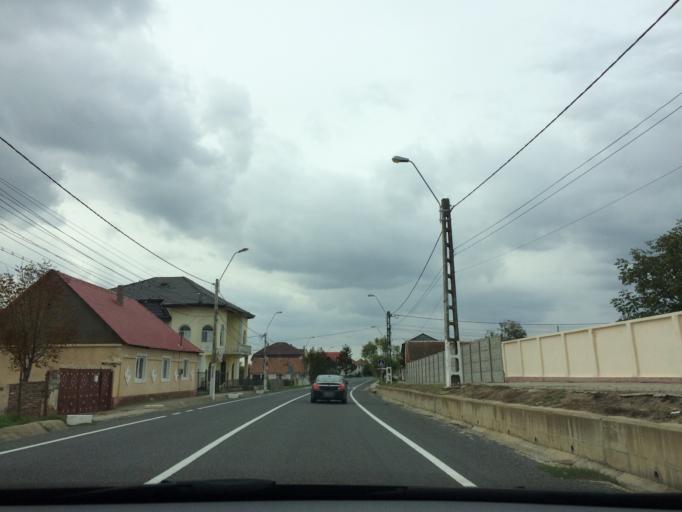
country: RO
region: Timis
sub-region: Oras Recas
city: Recas
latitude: 45.7983
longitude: 21.4979
